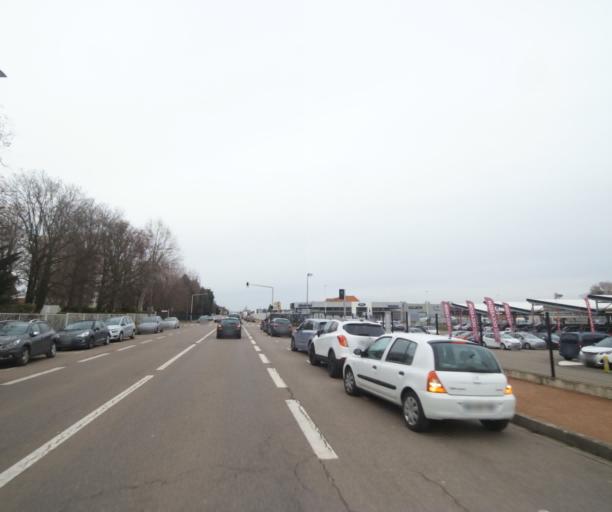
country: FR
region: Rhone-Alpes
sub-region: Departement de la Loire
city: Le Coteau
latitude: 46.0433
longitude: 4.0827
